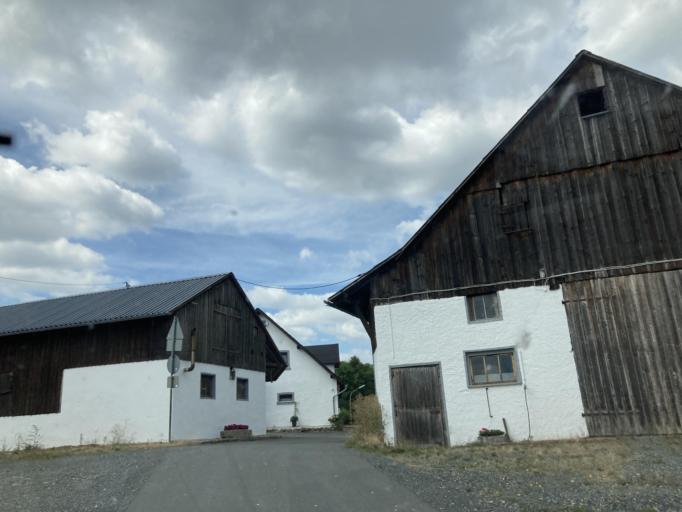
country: DE
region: Bavaria
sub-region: Upper Franconia
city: Grafengehaig
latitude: 50.1830
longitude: 11.5579
